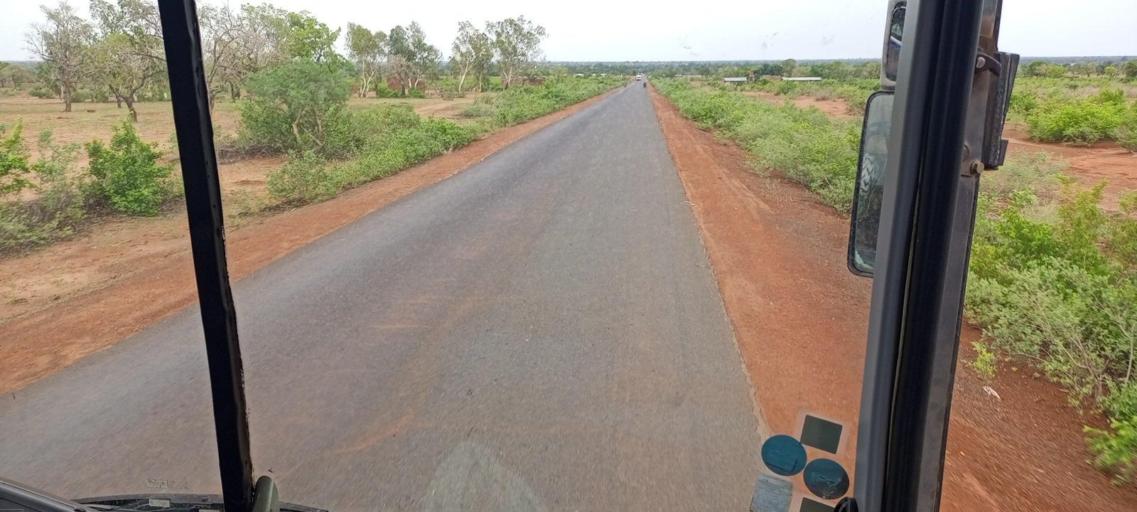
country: ML
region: Segou
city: Bla
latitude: 12.6958
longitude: -5.7239
